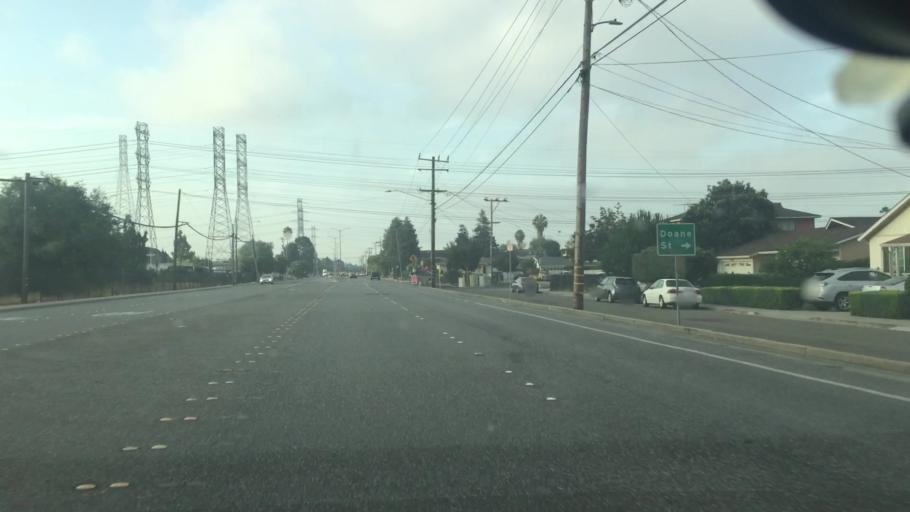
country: US
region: California
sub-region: Alameda County
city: Fremont
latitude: 37.5162
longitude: -121.9536
